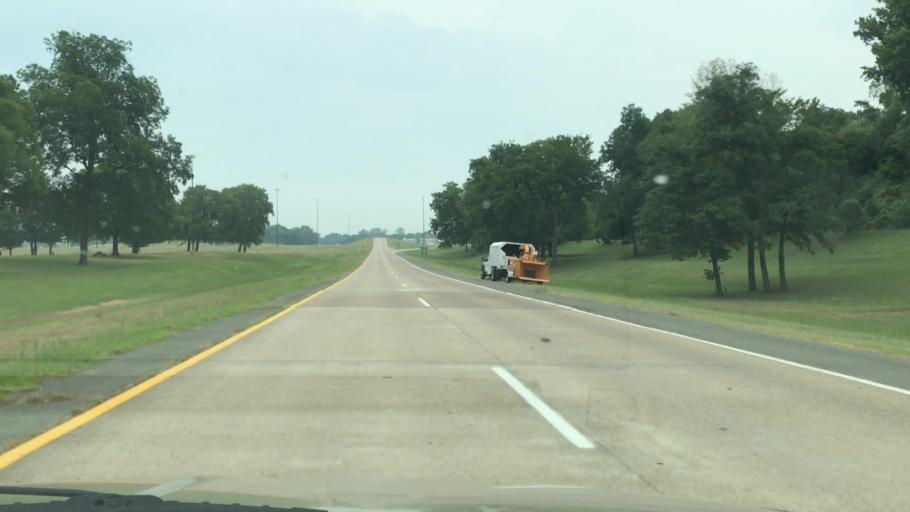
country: US
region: Louisiana
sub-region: Bossier Parish
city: Bossier City
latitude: 32.5044
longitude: -93.7207
